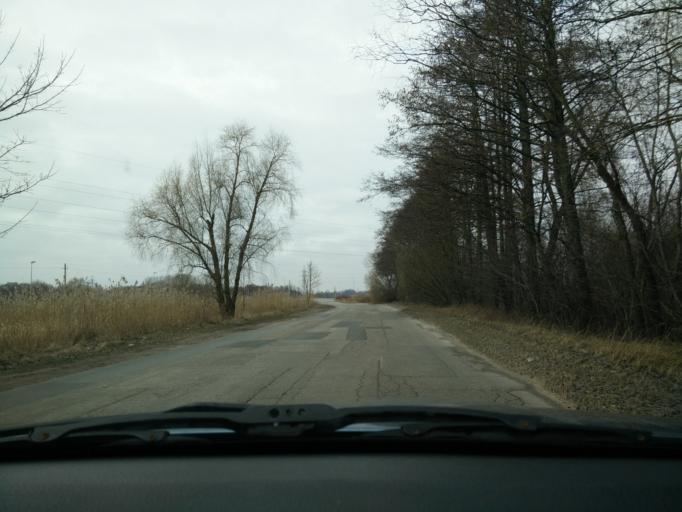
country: LT
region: Klaipedos apskritis
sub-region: Klaipeda
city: Klaipeda
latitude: 55.7239
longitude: 21.1687
